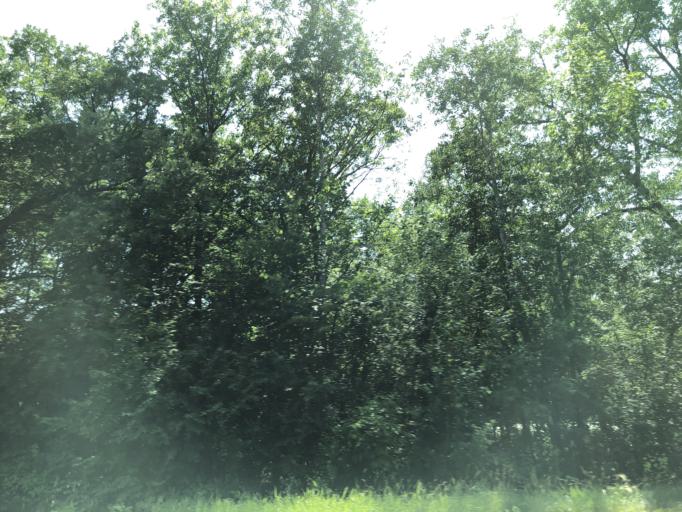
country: US
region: Minnesota
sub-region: Douglas County
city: Alexandria
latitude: 45.9304
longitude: -95.3755
